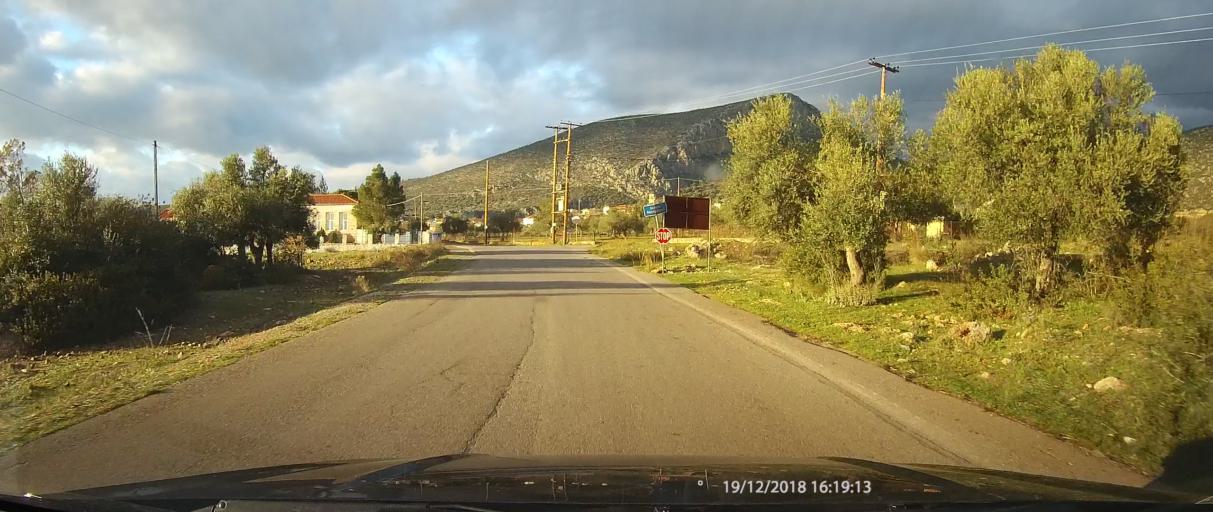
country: GR
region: Peloponnese
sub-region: Nomos Lakonias
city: Kato Glikovrisi
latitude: 36.9308
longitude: 22.8228
